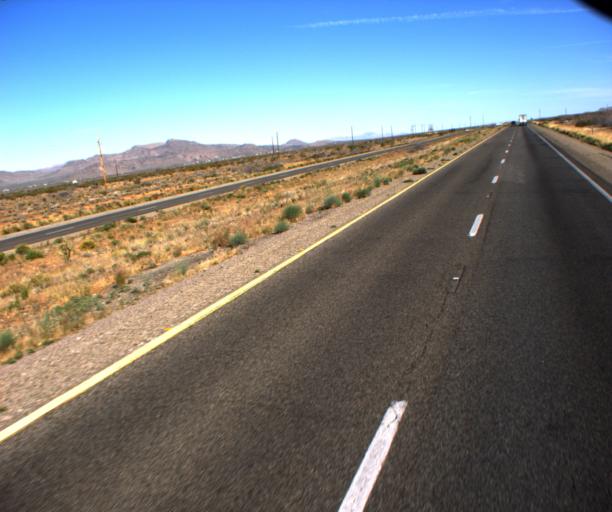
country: US
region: Arizona
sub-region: Mohave County
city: Golden Valley
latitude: 35.3125
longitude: -114.1981
